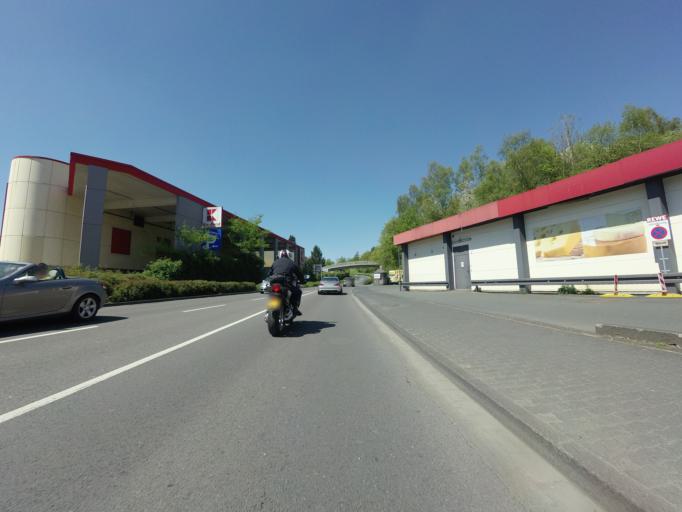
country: DE
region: North Rhine-Westphalia
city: Kreuztal
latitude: 50.9619
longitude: 7.9958
